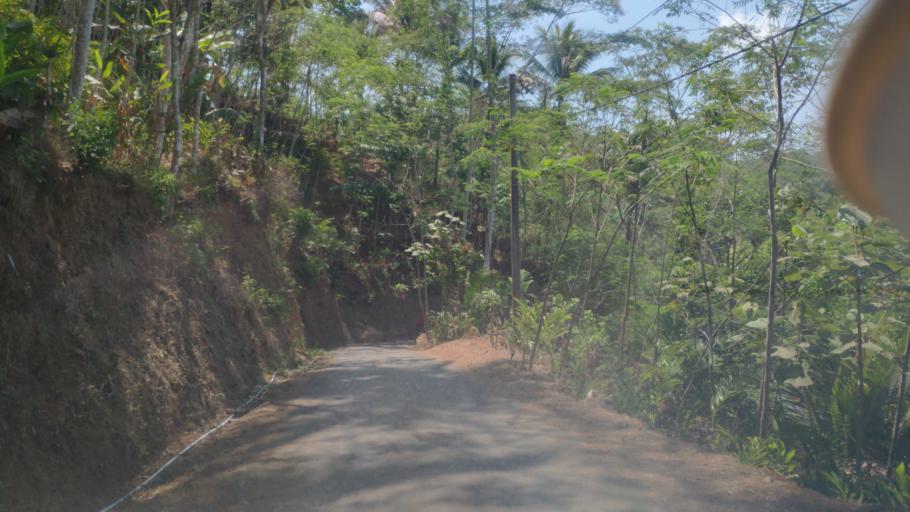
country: ID
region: Central Java
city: Wonosobo
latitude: -7.4351
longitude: 109.6880
